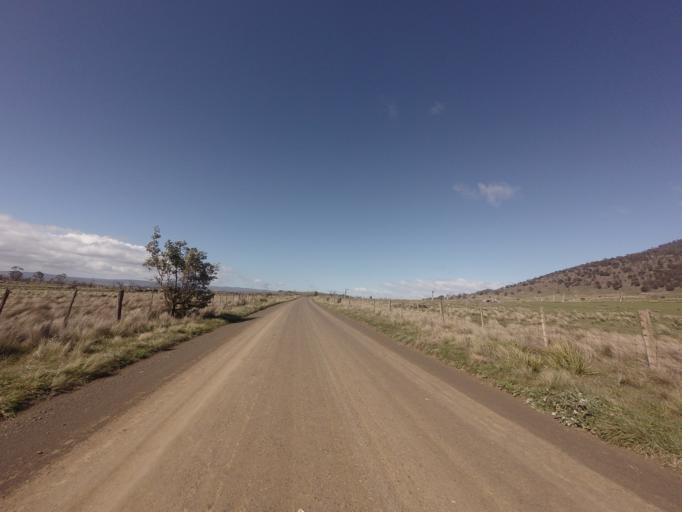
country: AU
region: Tasmania
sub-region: Northern Midlands
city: Evandale
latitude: -41.9235
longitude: 147.4053
